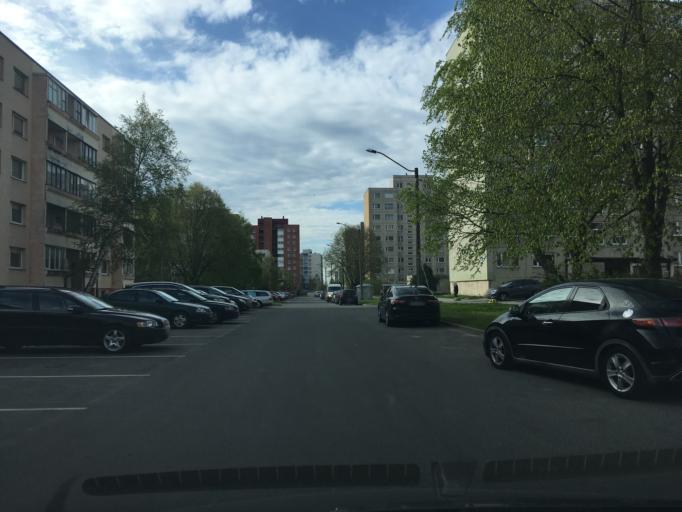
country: EE
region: Harju
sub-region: Tallinna linn
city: Kose
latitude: 59.4428
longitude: 24.8389
